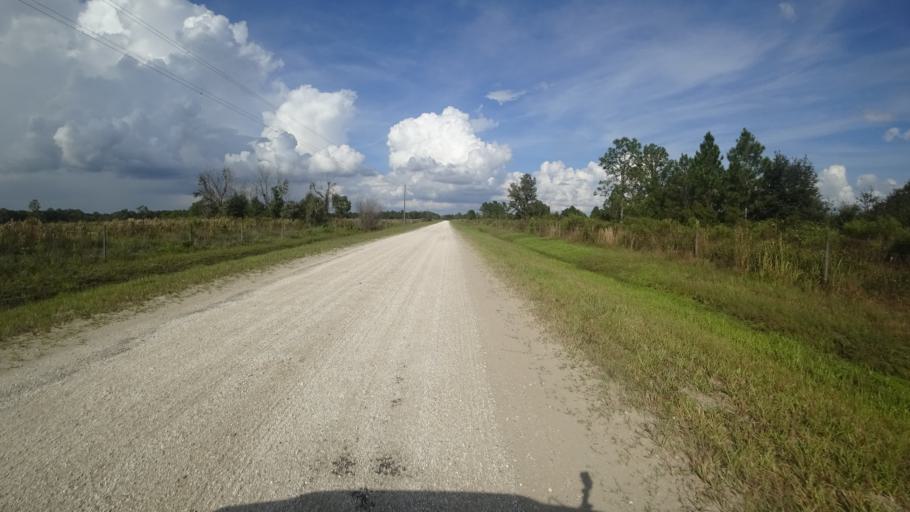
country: US
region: Florida
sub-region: Hillsborough County
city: Wimauma
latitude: 27.5969
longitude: -82.1215
